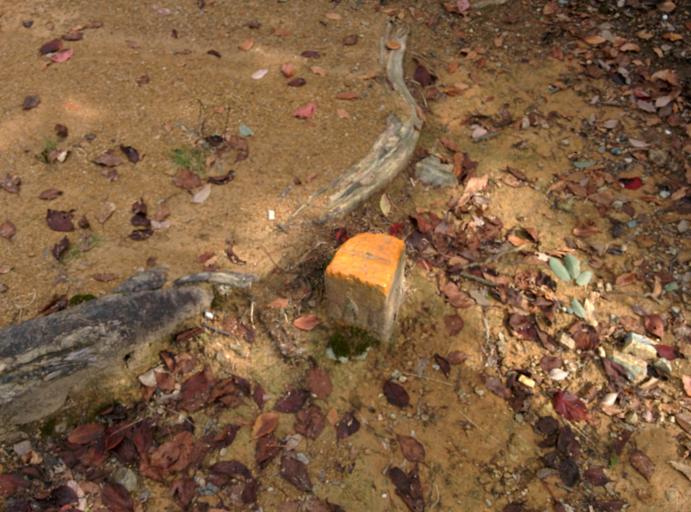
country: JP
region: Kyoto
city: Kyoto
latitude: 35.0331
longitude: 135.7155
